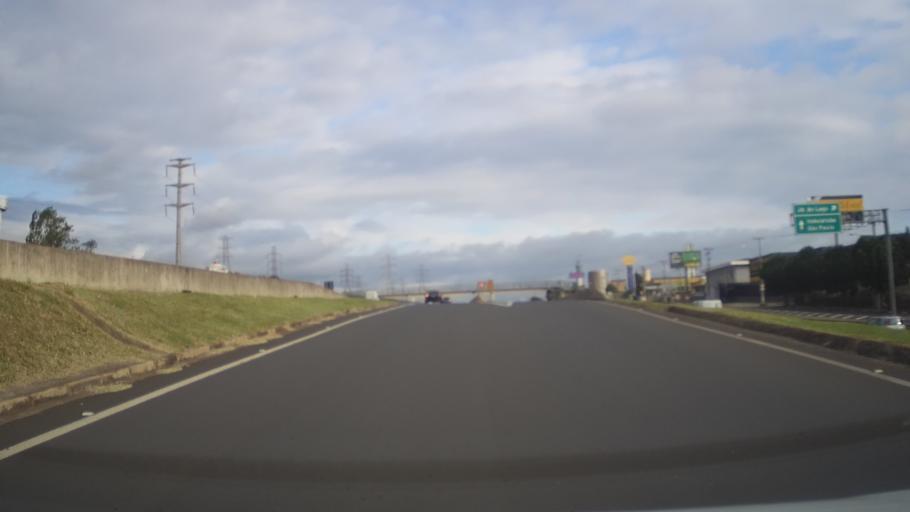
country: BR
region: Sao Paulo
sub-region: Campinas
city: Campinas
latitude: -22.9285
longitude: -47.0813
